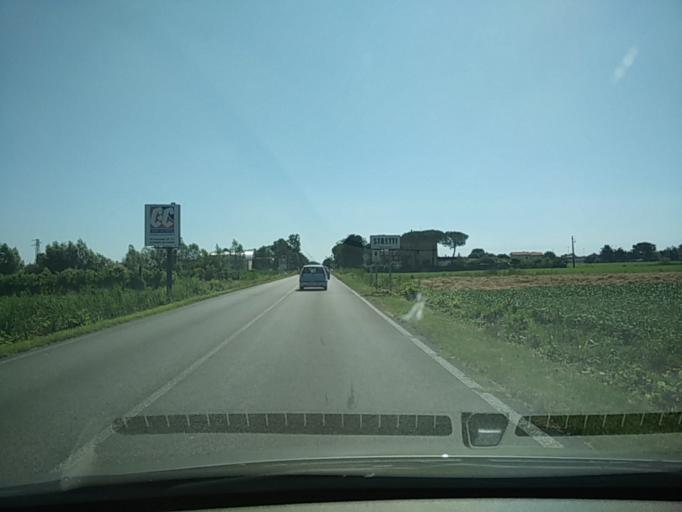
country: IT
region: Veneto
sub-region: Provincia di Venezia
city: Crepaldo
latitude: 45.6365
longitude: 12.6781
